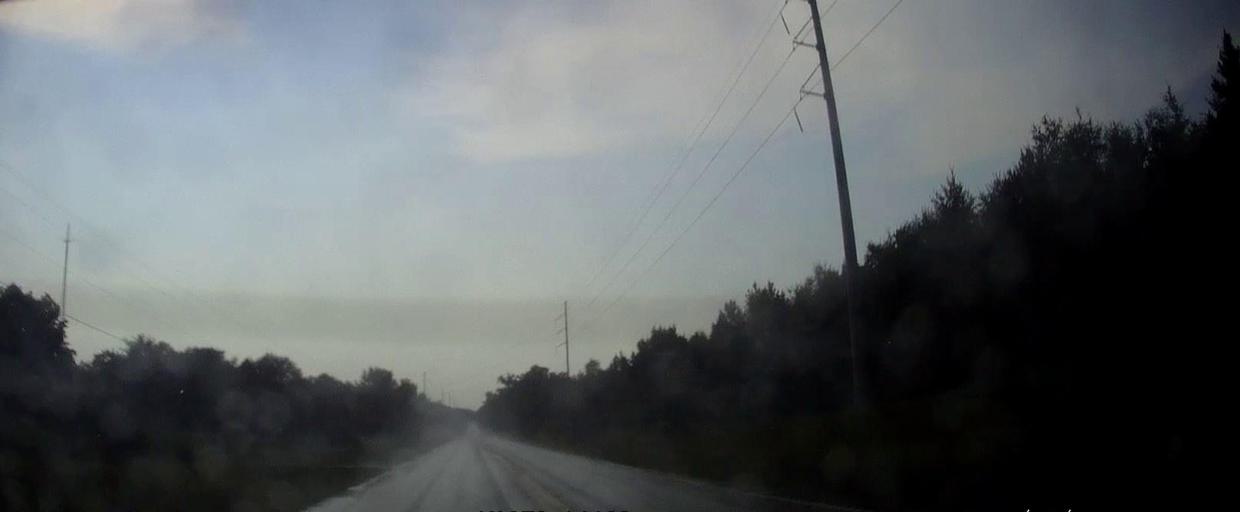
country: US
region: Georgia
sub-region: Twiggs County
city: Jeffersonville
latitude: 32.5778
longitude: -83.2073
